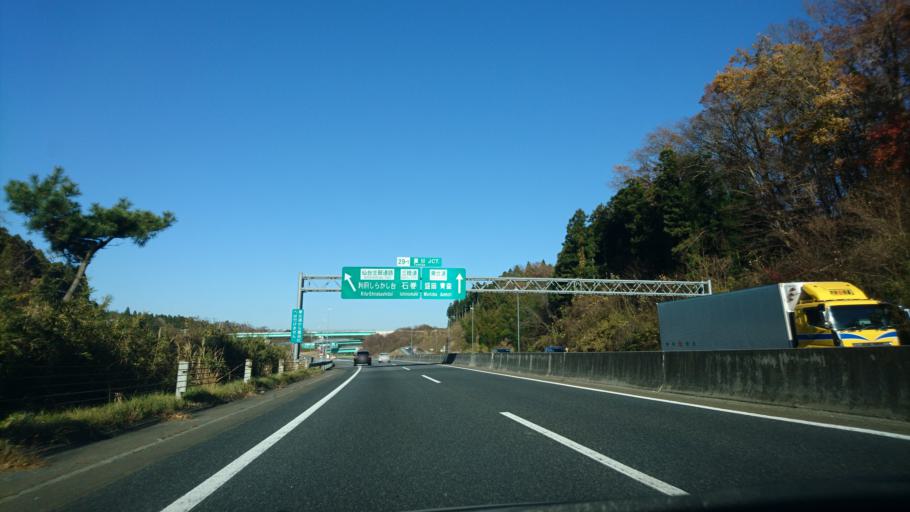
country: JP
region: Miyagi
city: Tomiya
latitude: 38.3688
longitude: 140.8855
